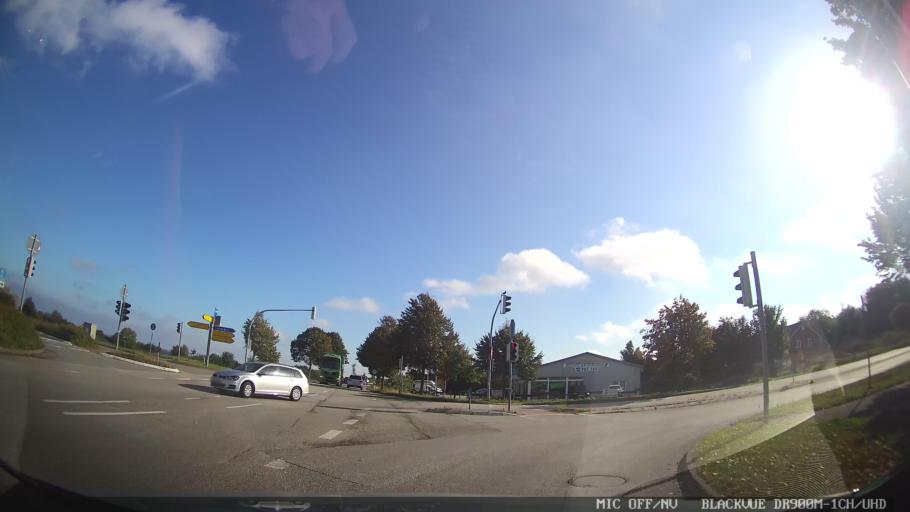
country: DE
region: Schleswig-Holstein
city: Heiligenhafen
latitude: 54.3645
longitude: 11.0085
